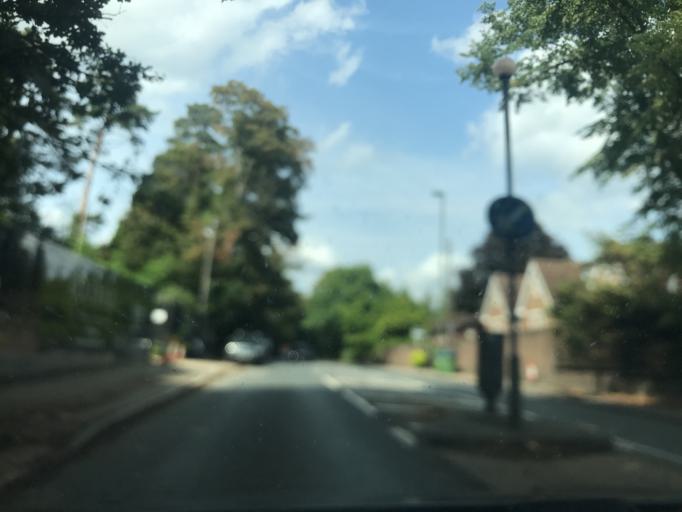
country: GB
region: England
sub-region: Surrey
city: Weybridge
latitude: 51.3579
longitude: -0.4569
